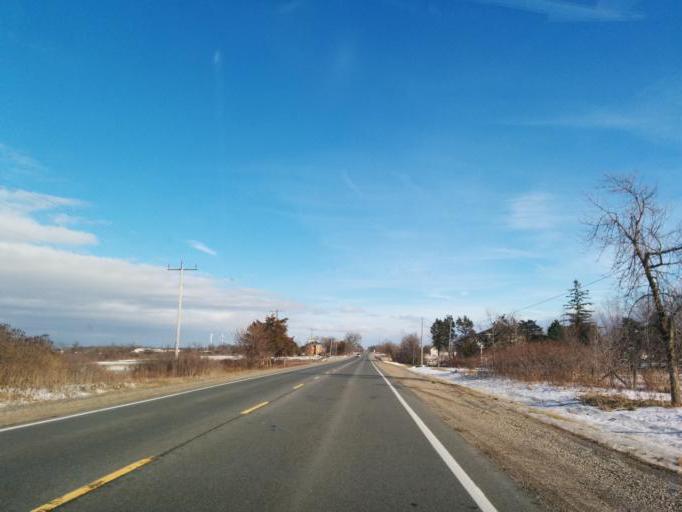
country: CA
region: Ontario
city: Ancaster
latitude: 42.9306
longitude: -79.9385
